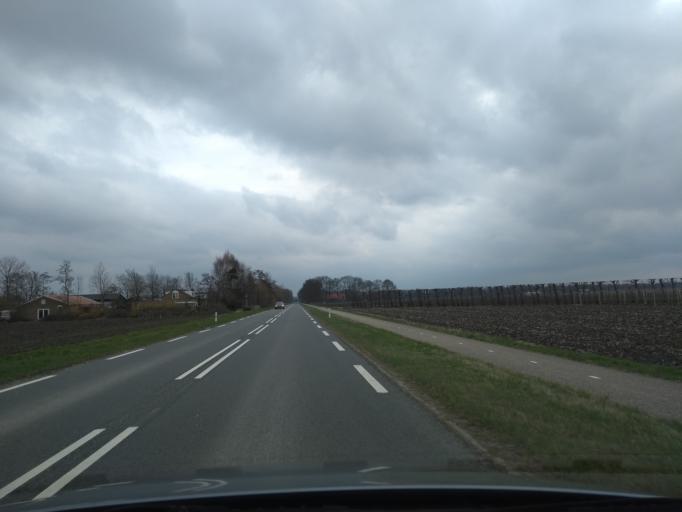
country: NL
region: Flevoland
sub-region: Gemeente Noordoostpolder
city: Ens
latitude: 52.7270
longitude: 5.8633
